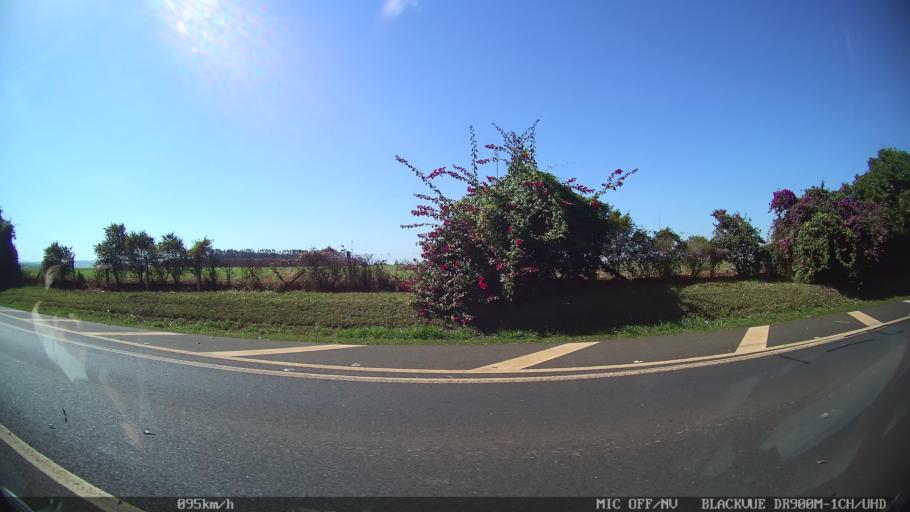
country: BR
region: Sao Paulo
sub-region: Batatais
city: Batatais
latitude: -20.7484
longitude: -47.5313
